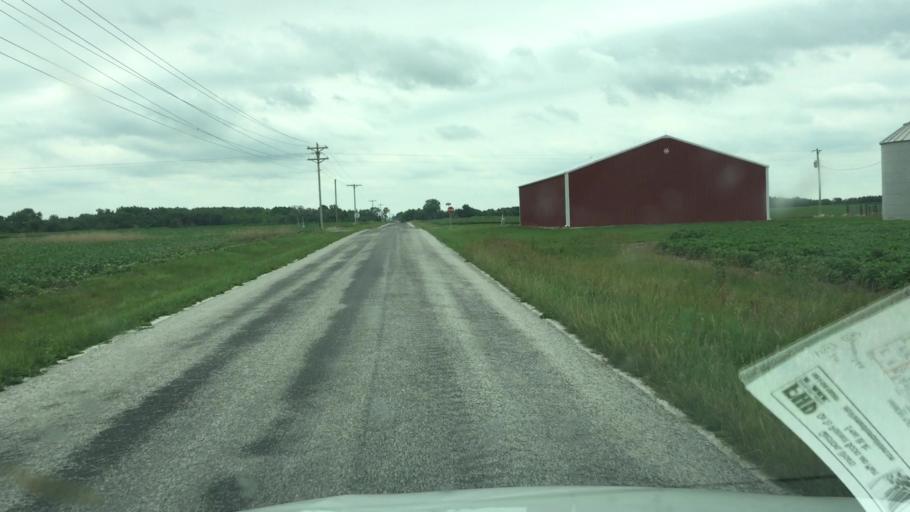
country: US
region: Illinois
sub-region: Hancock County
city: Carthage
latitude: 40.2912
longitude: -91.0834
